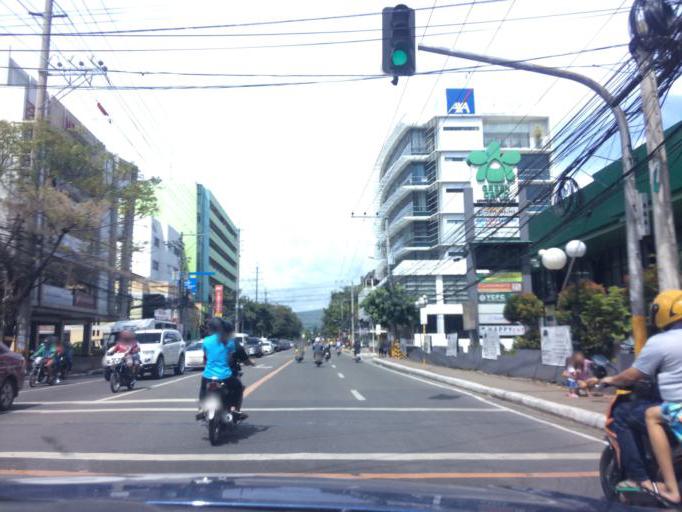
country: PH
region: Central Visayas
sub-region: Province of Cebu
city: Cebu City
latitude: 10.3172
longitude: 123.8934
